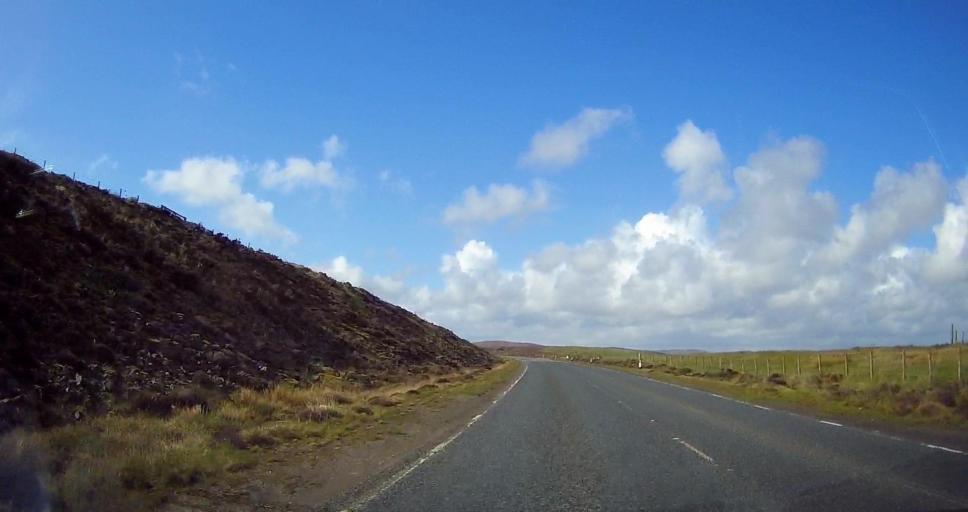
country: GB
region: Scotland
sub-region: Shetland Islands
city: Lerwick
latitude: 60.2222
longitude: -1.2343
